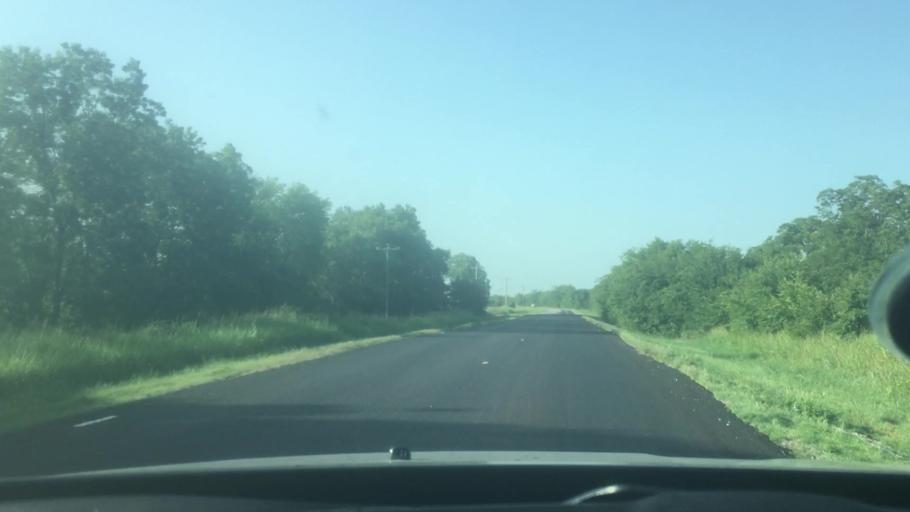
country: US
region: Oklahoma
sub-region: Coal County
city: Coalgate
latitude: 34.3546
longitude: -96.4246
